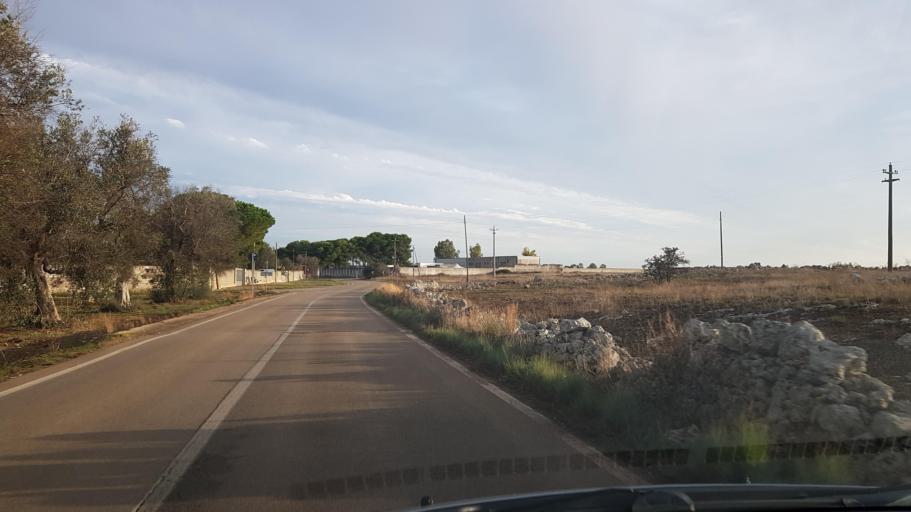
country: IT
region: Apulia
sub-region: Provincia di Lecce
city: Surbo
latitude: 40.4277
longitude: 18.1178
